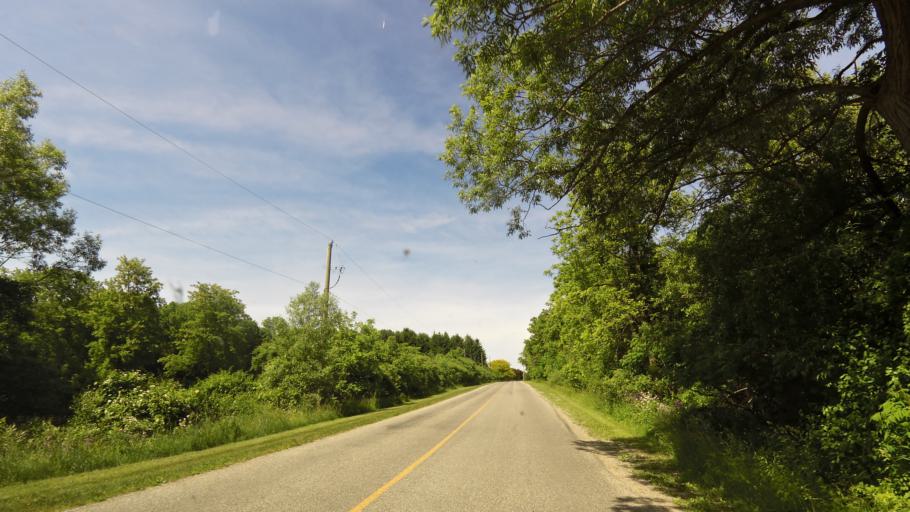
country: CA
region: Ontario
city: Norfolk County
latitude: 42.7273
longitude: -80.2925
